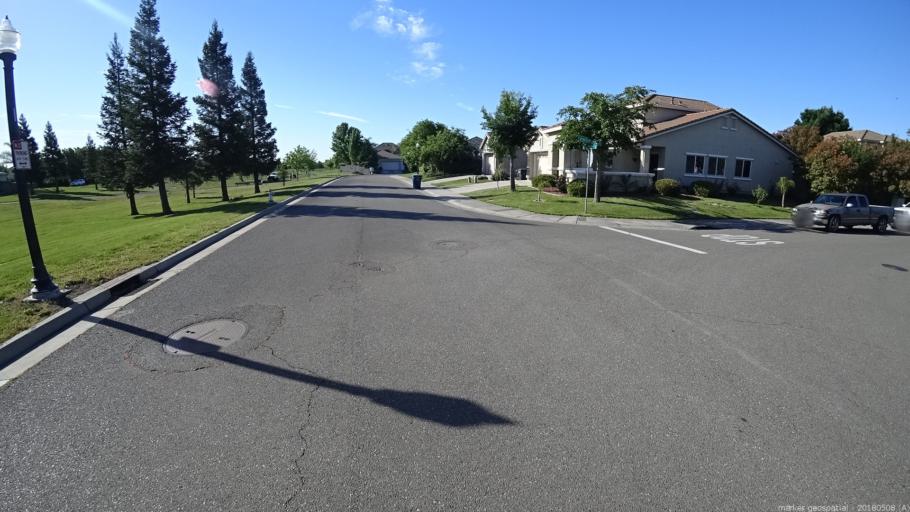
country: US
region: California
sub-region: Sacramento County
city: Elverta
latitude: 38.6799
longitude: -121.5021
